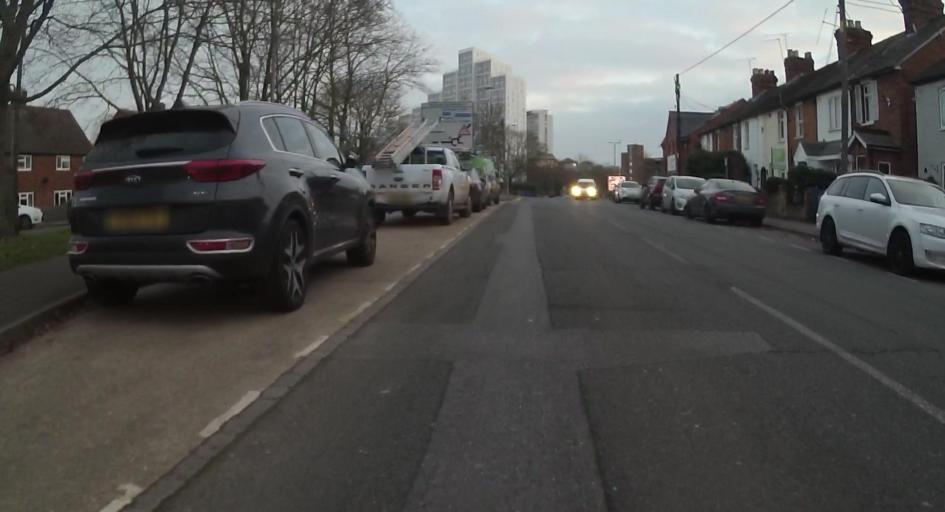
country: GB
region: England
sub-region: Bracknell Forest
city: Bracknell
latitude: 51.4195
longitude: -0.7563
